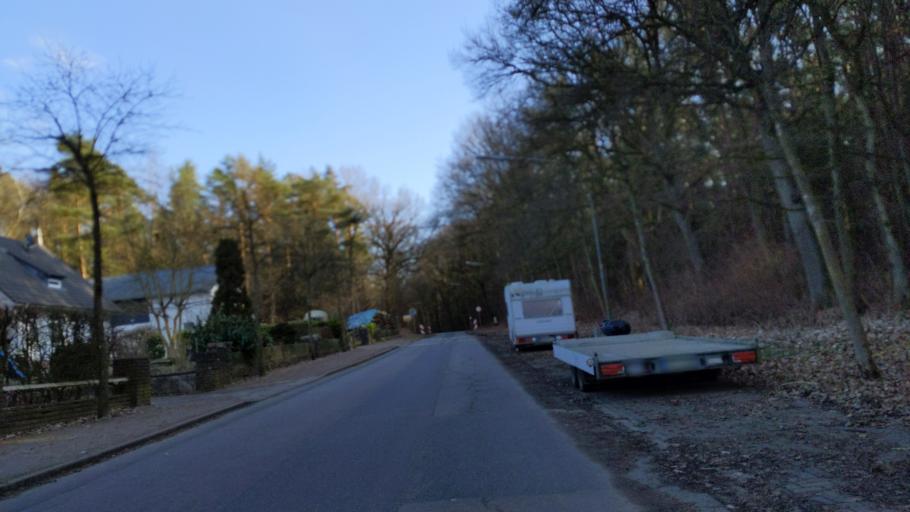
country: DE
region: Schleswig-Holstein
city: Ratekau
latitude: 53.9701
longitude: 10.7043
